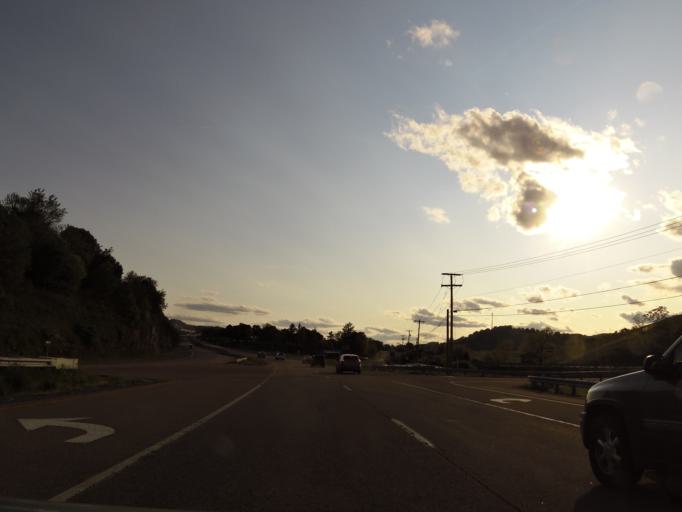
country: US
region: Virginia
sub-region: Russell County
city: Lebanon
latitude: 36.9096
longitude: -82.0340
